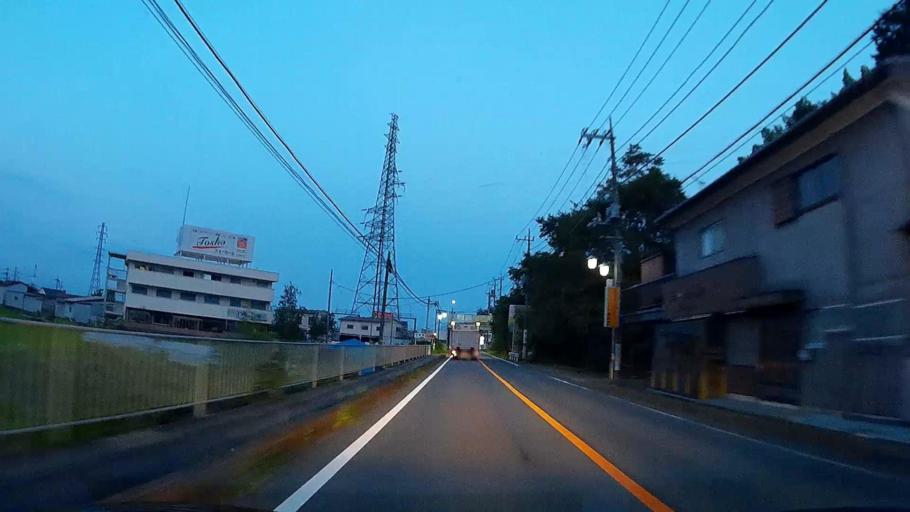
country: JP
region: Gunma
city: Annaka
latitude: 36.3477
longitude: 138.9527
